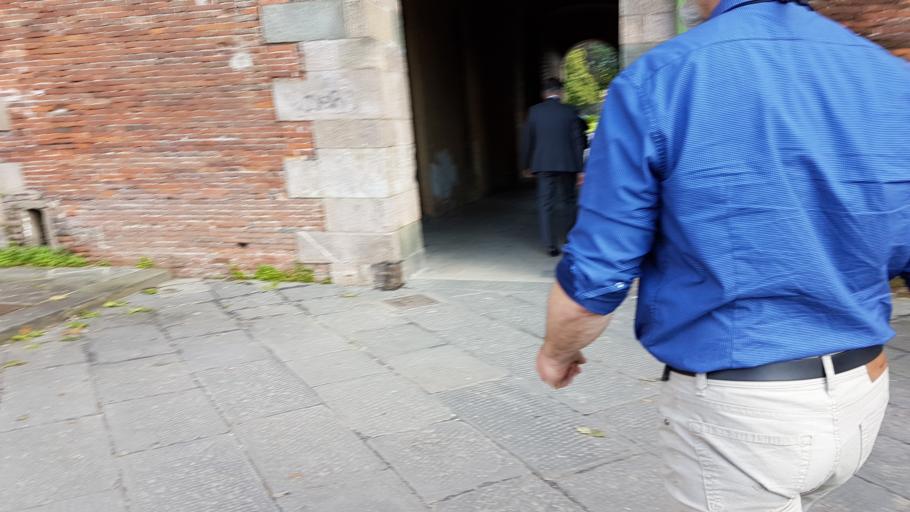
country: IT
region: Tuscany
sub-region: Provincia di Lucca
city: Lucca
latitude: 43.8392
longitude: 10.5029
